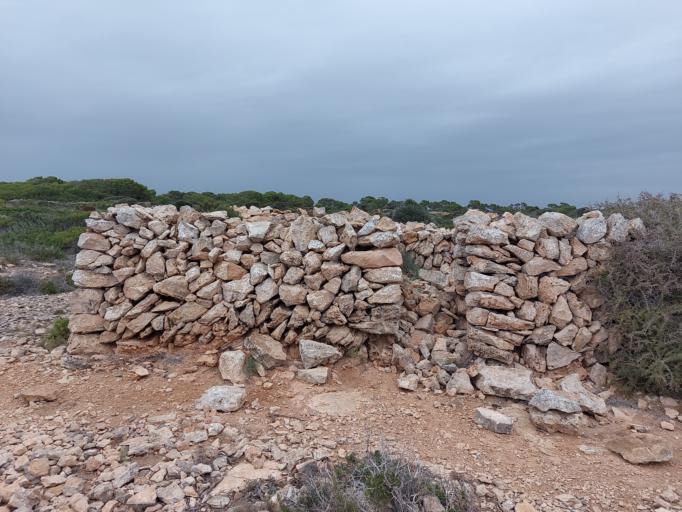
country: ES
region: Balearic Islands
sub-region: Illes Balears
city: Llucmajor
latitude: 39.3618
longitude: 2.8144
